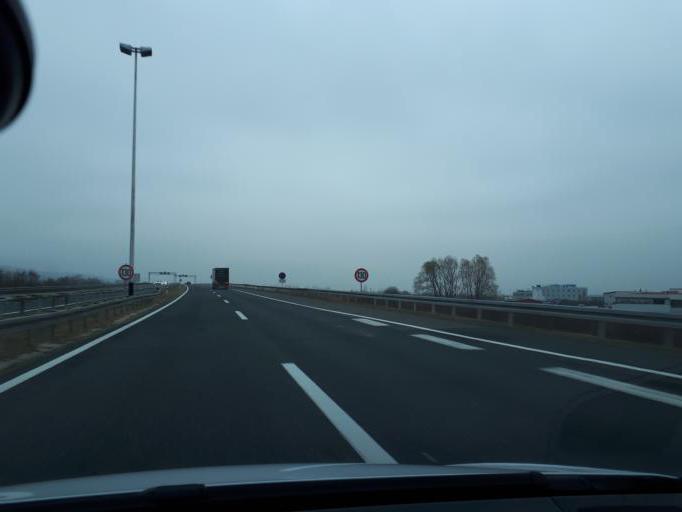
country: HR
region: Brodsko-Posavska
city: Slobodnica
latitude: 45.1711
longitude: 17.9459
